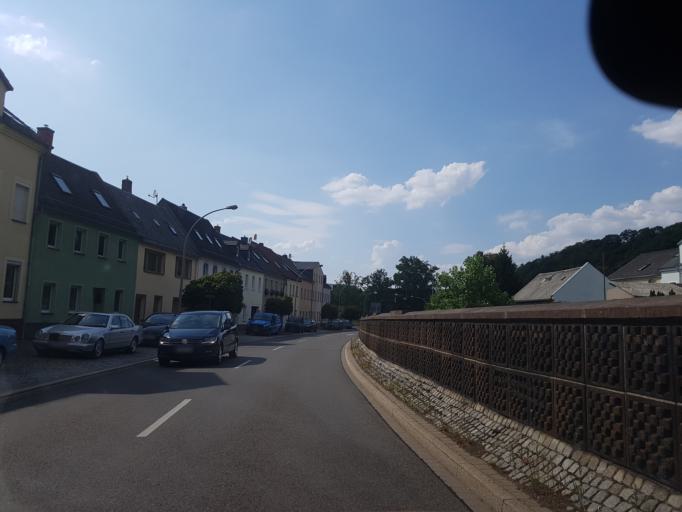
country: DE
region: Saxony
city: Waldheim
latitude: 51.0762
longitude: 13.0300
